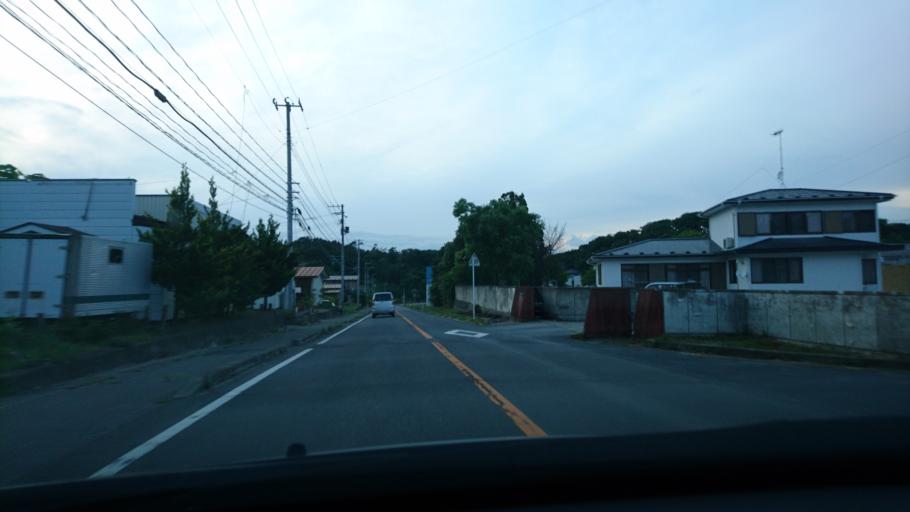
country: JP
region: Miyagi
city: Furukawa
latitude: 38.7570
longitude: 141.0056
